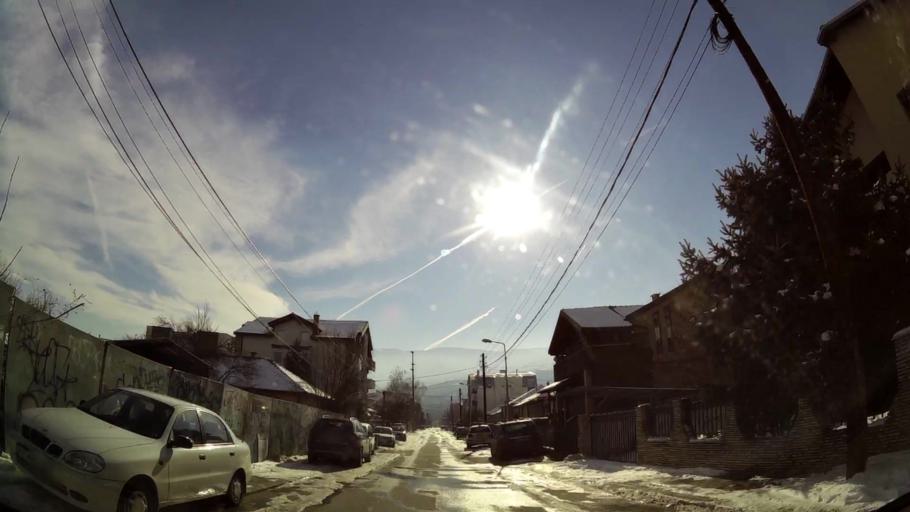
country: MK
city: Krushopek
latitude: 42.0036
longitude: 21.3689
